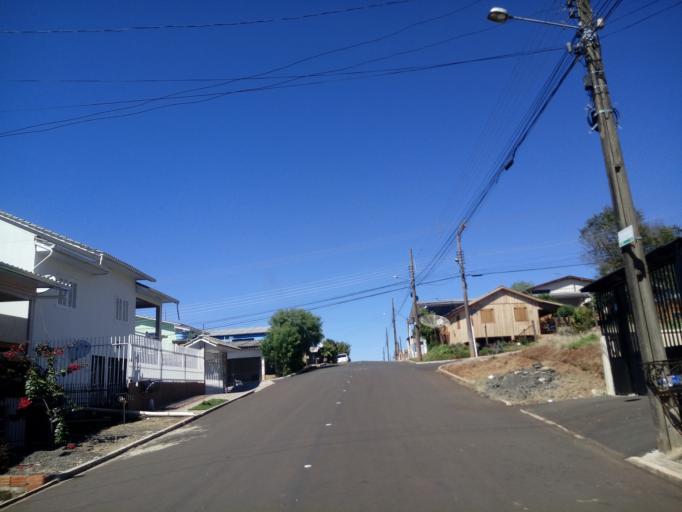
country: BR
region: Santa Catarina
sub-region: Chapeco
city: Chapeco
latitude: -27.0921
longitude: -52.6733
